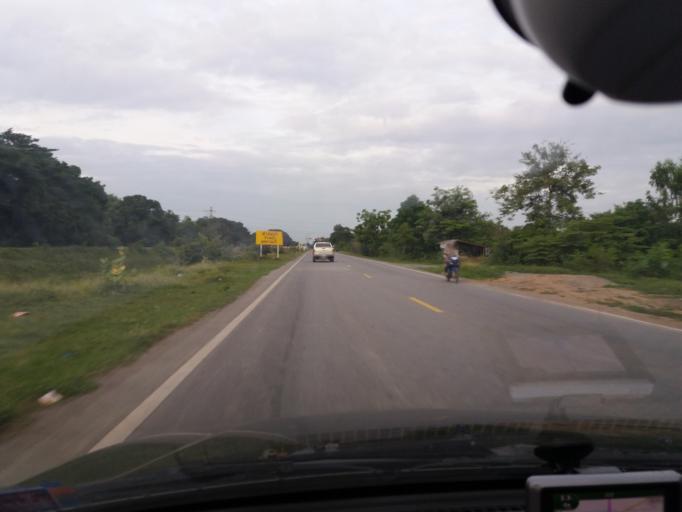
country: TH
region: Suphan Buri
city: Don Chedi
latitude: 14.5352
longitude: 99.9342
